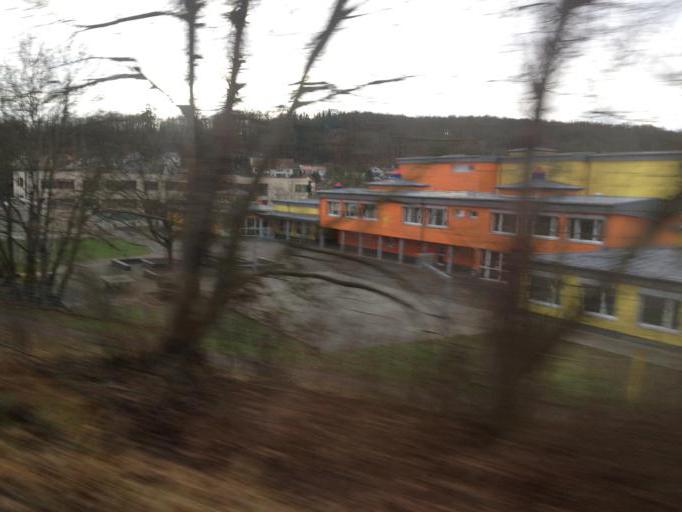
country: DE
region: Hesse
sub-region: Regierungsbezirk Giessen
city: Lich
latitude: 50.5181
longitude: 8.8116
